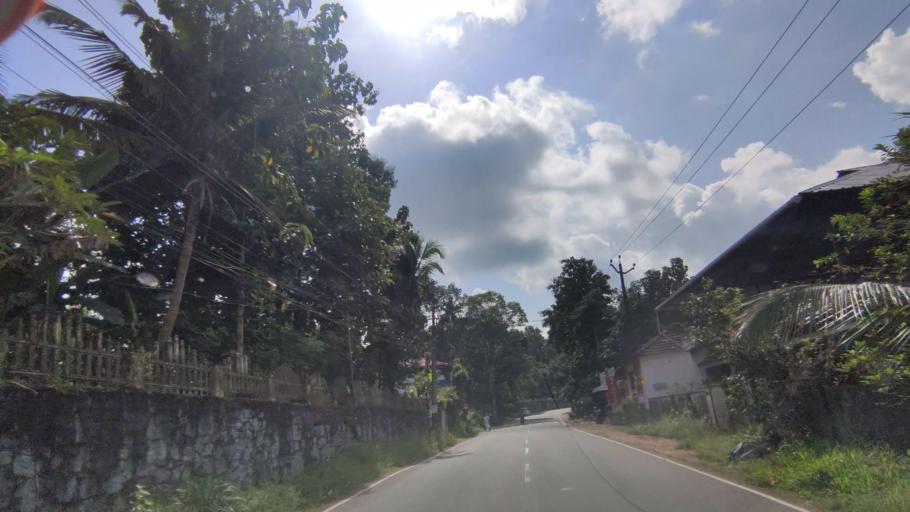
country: IN
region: Kerala
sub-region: Kottayam
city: Kottayam
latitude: 9.6750
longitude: 76.5519
